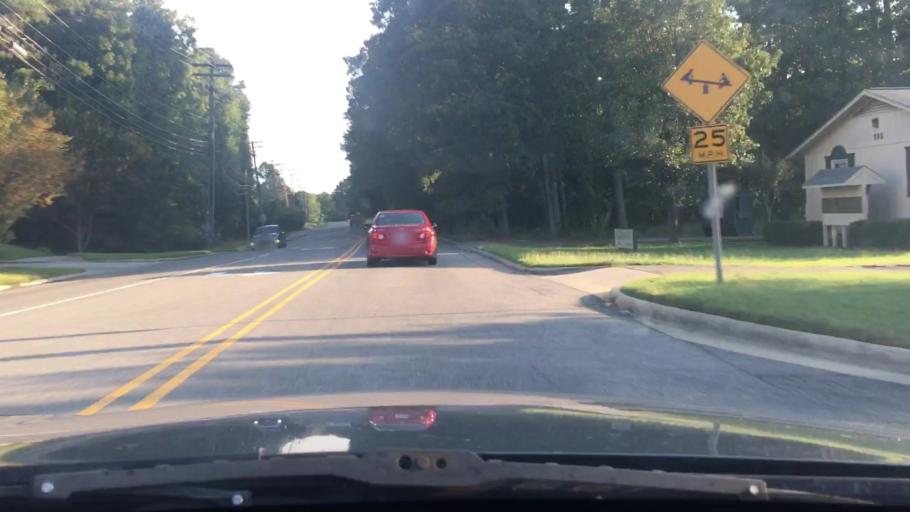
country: US
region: North Carolina
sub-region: Durham County
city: Durham
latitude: 36.0088
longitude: -78.9547
